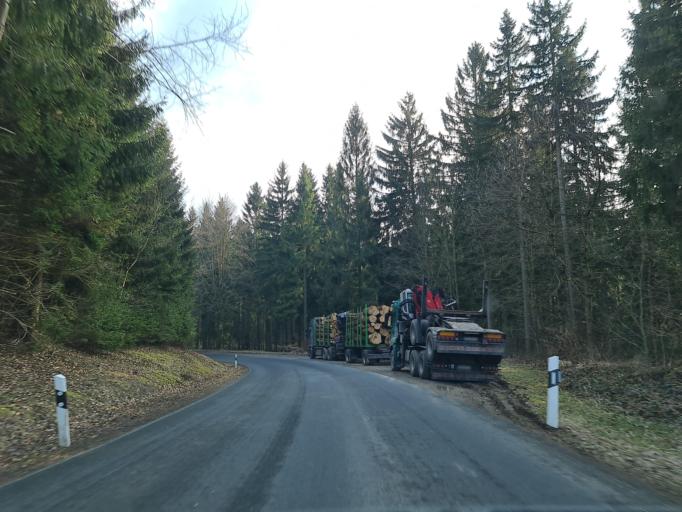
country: DE
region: Saxony
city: Rodewisch
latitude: 50.4972
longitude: 12.4516
